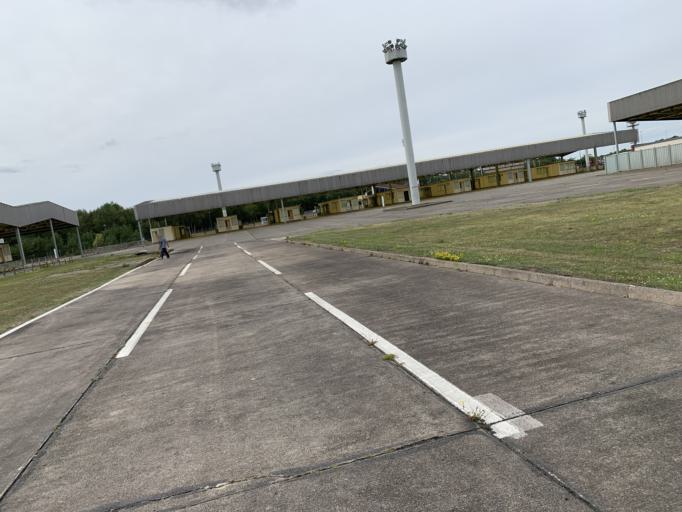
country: DE
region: Saxony-Anhalt
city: Beendorf
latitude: 52.2144
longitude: 11.0839
